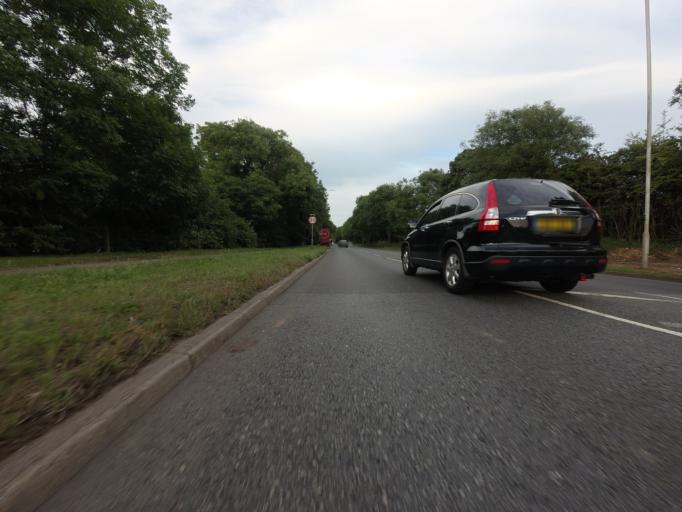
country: GB
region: England
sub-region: Greater London
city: Sidcup
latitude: 51.4134
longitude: 0.1162
